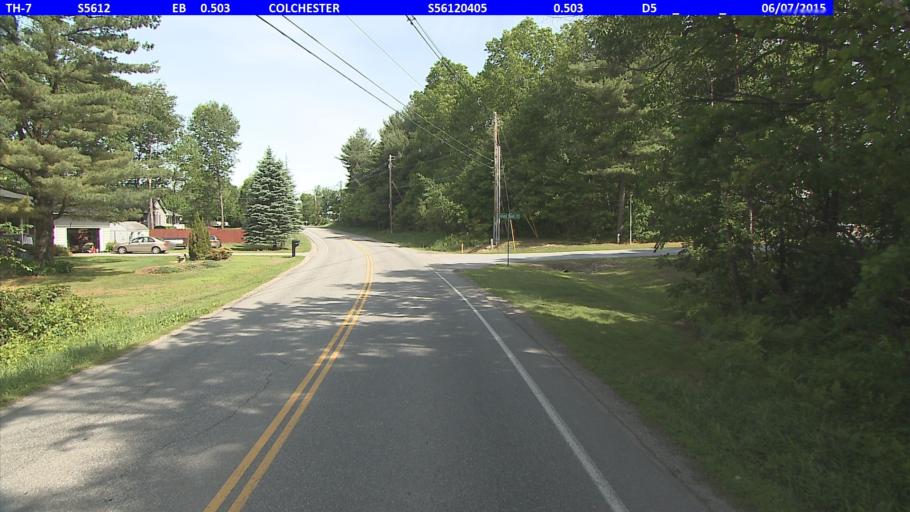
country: US
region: Vermont
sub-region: Chittenden County
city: Colchester
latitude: 44.5176
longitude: -73.1479
